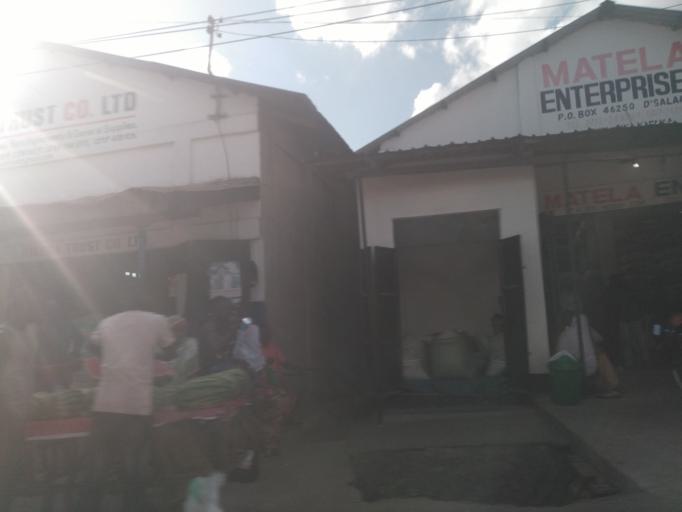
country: TZ
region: Dar es Salaam
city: Dar es Salaam
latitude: -6.8717
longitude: 39.2605
